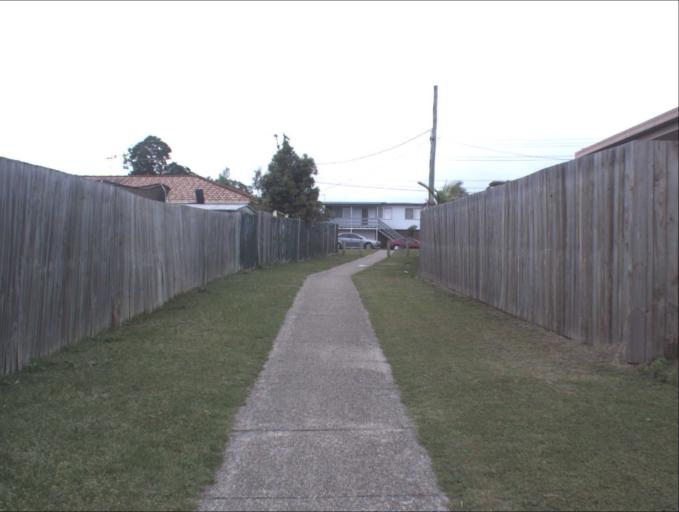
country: AU
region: Queensland
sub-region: Logan
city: Waterford West
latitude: -27.6857
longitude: 153.1136
